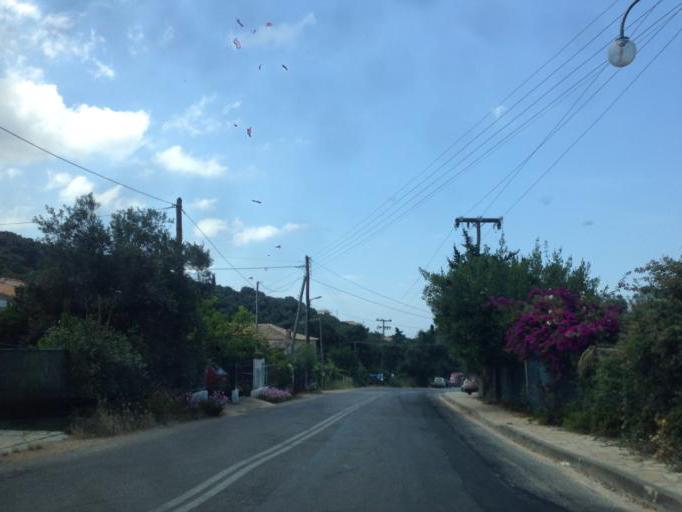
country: GR
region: Ionian Islands
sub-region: Nomos Kerkyras
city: Acharavi
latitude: 39.7842
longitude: 19.9220
